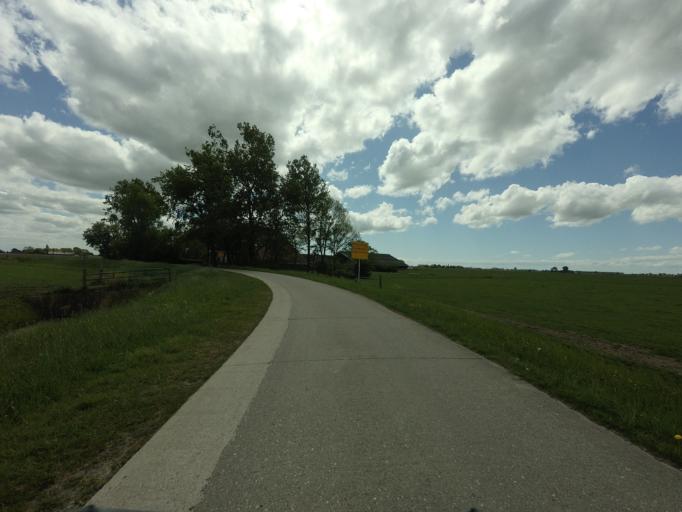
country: NL
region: Friesland
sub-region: Gemeente Littenseradiel
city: Wommels
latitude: 53.1200
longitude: 5.5523
